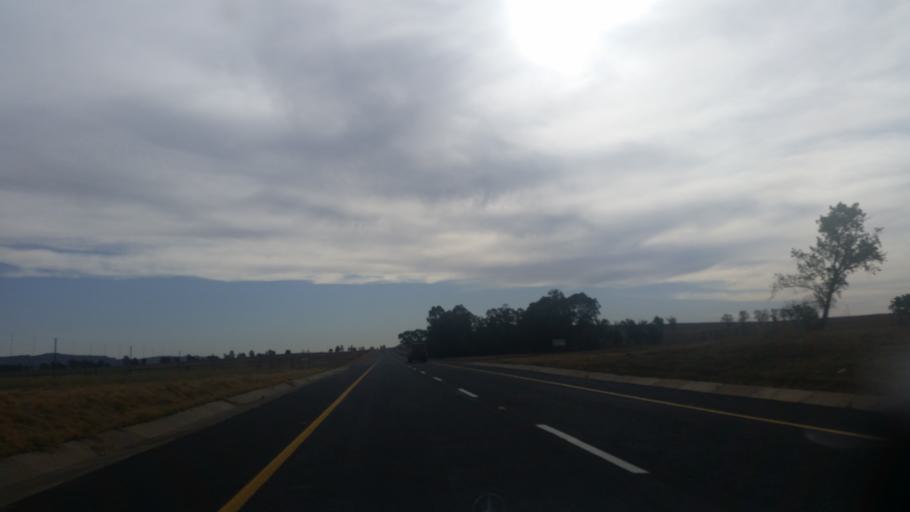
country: ZA
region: Orange Free State
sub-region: Thabo Mofutsanyana District Municipality
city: Phuthaditjhaba
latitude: -28.3125
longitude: 28.7536
